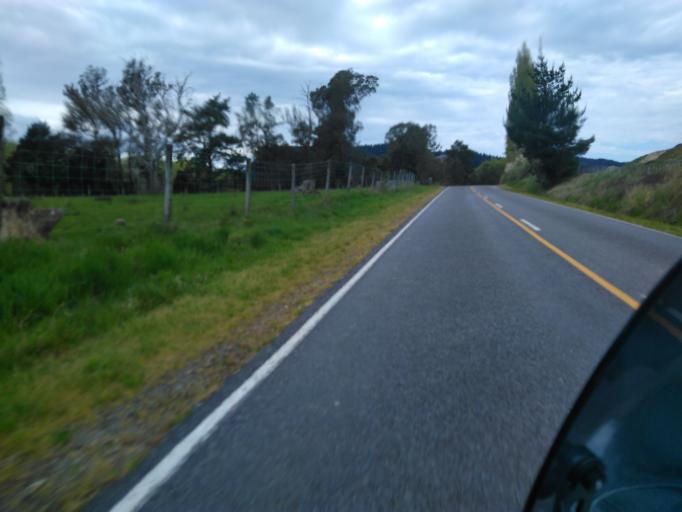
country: NZ
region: Hawke's Bay
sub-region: Wairoa District
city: Wairoa
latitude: -38.8990
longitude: 177.4671
